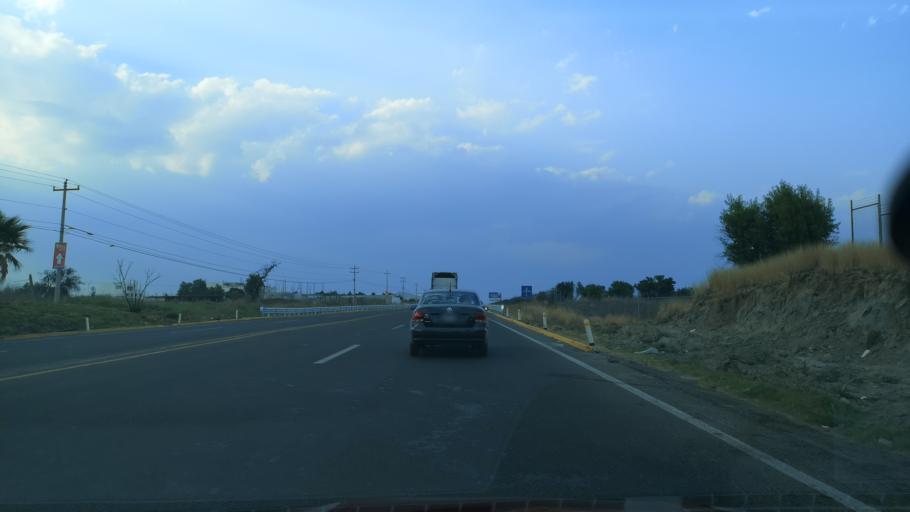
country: MX
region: Puebla
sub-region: Juan C. Bonilla
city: Santa Maria Zacatepec
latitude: 19.1359
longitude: -98.3736
